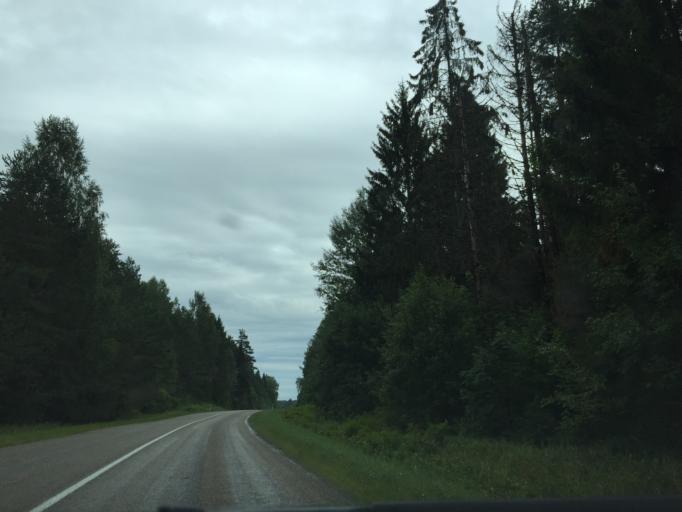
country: LV
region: Dagda
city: Dagda
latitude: 56.1856
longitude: 27.3712
